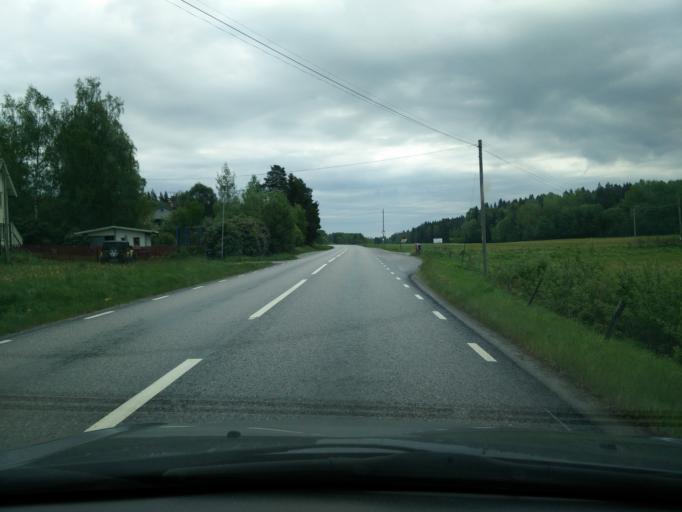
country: SE
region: Stockholm
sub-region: Norrtalje Kommun
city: Norrtalje
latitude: 59.7838
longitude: 18.7804
